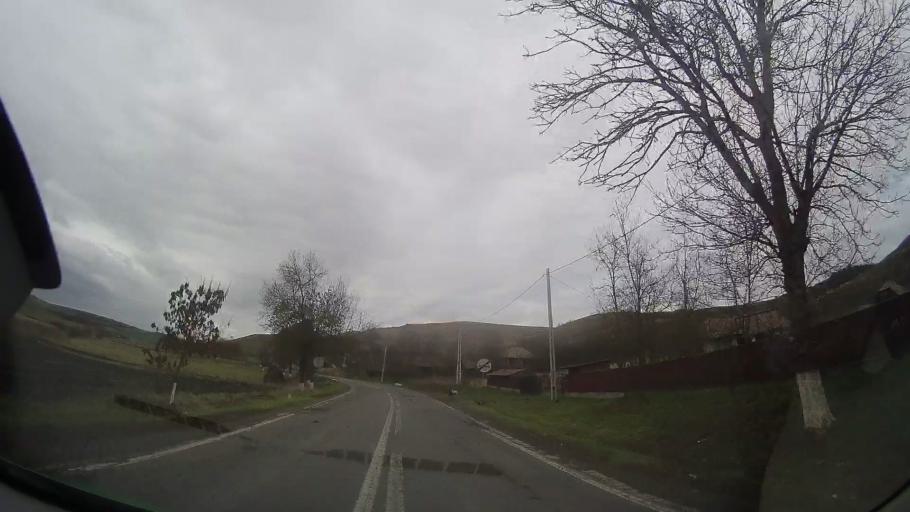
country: RO
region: Mures
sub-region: Comuna Craesti
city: Craiesti
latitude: 46.7604
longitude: 24.3957
